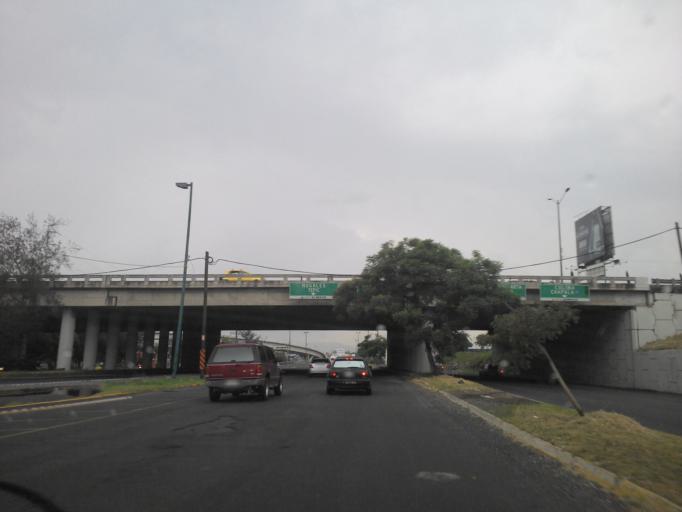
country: MX
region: Jalisco
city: Tlaquepaque
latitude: 20.6244
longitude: -103.3205
